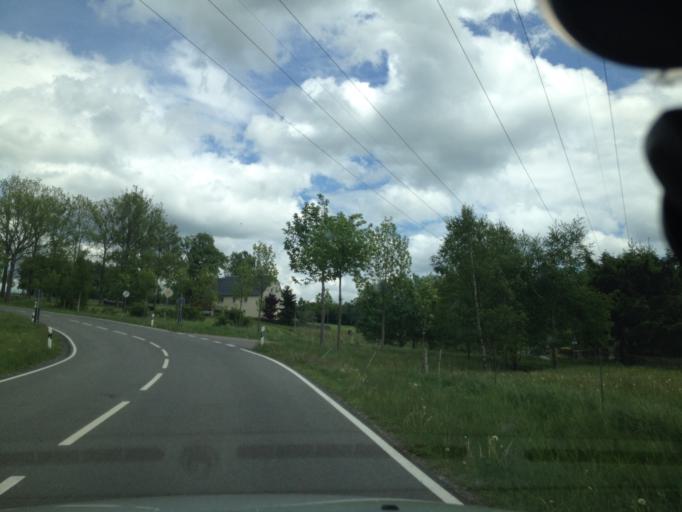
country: DE
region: Saxony
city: Barenstein
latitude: 50.5194
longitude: 13.0094
